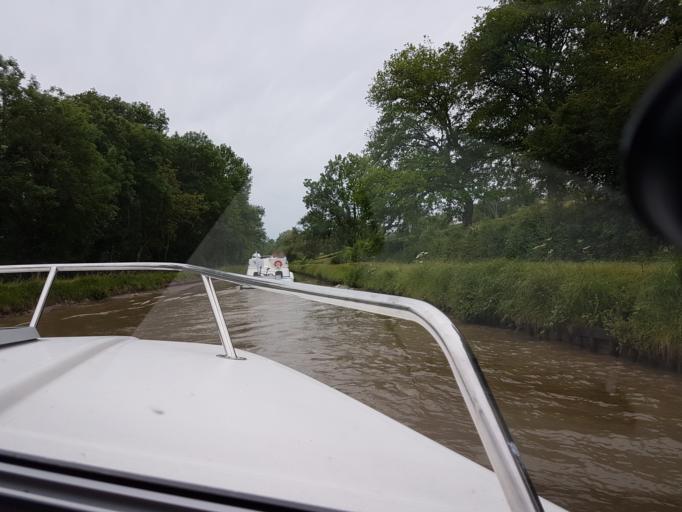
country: FR
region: Bourgogne
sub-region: Departement de la Nievre
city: Clamecy
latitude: 47.4010
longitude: 3.6050
